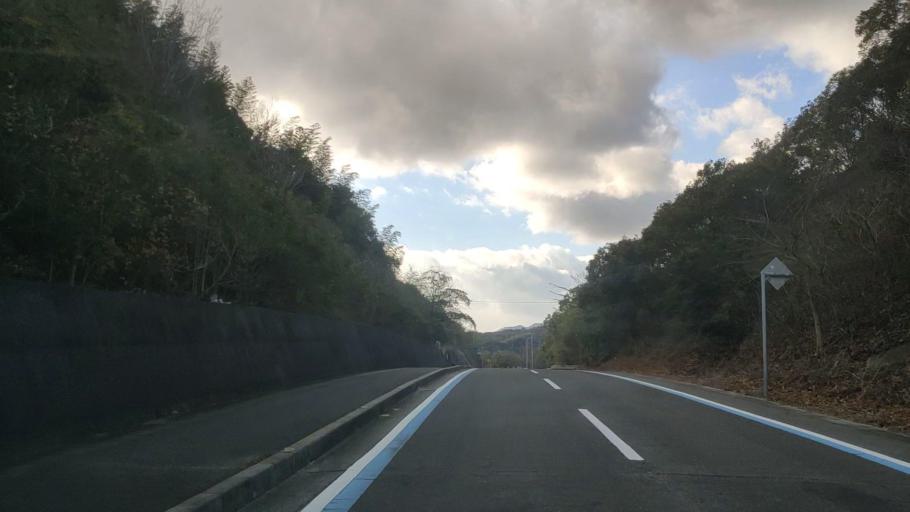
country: JP
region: Hiroshima
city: Innoshima
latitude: 34.2315
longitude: 133.0850
